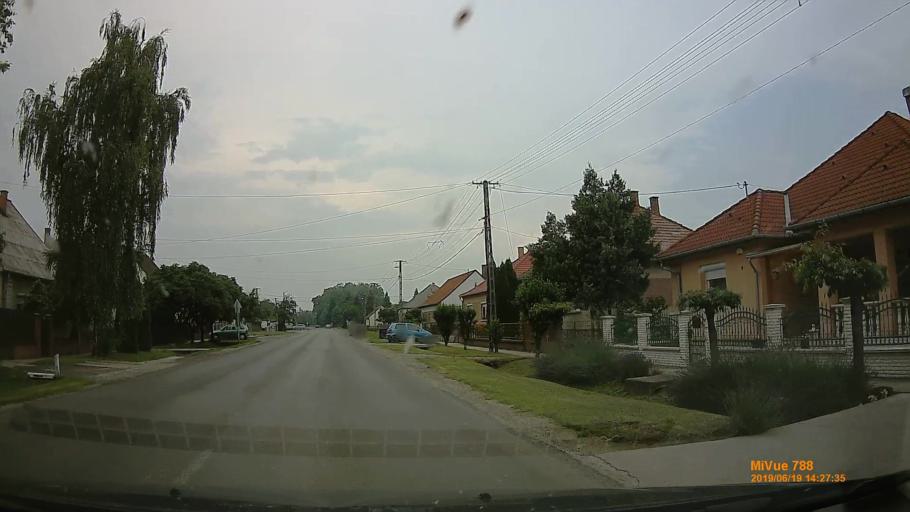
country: HU
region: Baranya
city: Szigetvar
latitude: 46.0441
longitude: 17.7818
